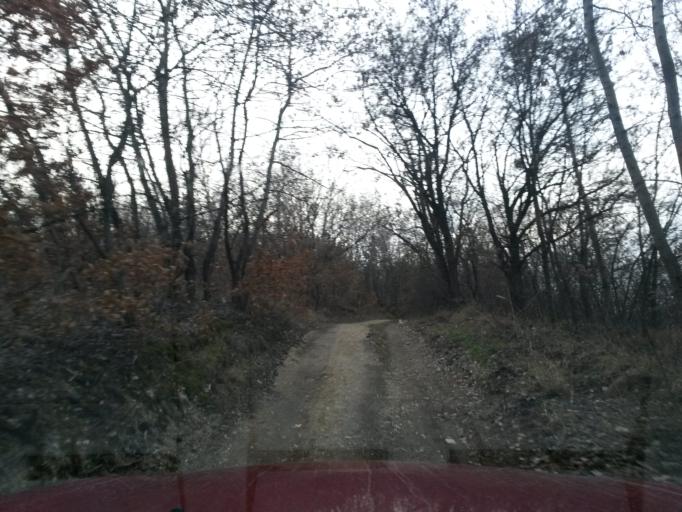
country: SK
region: Kosicky
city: Kosice
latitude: 48.7225
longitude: 21.2833
